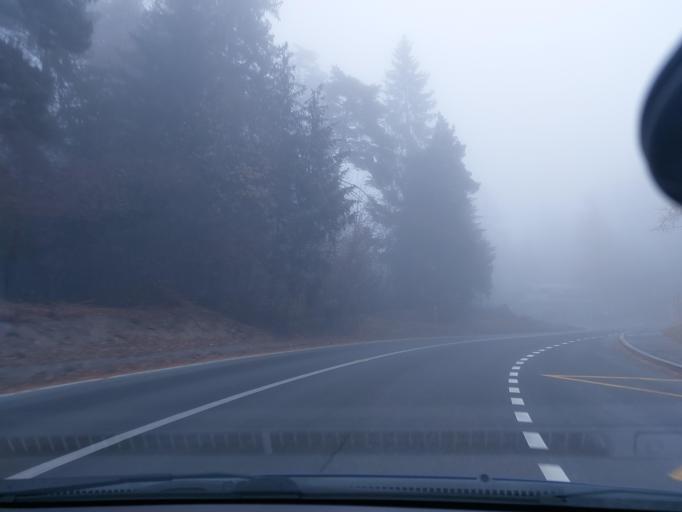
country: CH
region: Valais
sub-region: Sierre District
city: Lens
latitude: 46.2889
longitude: 7.4530
